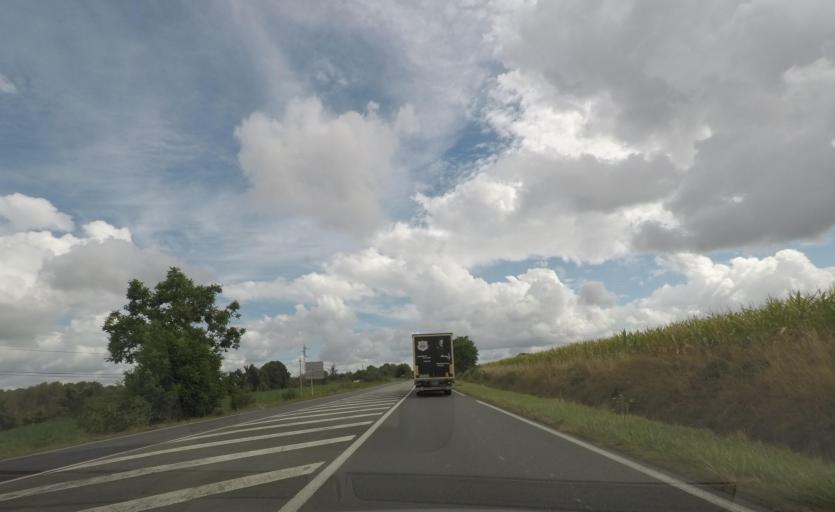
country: FR
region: Pays de la Loire
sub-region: Departement de Maine-et-Loire
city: Corze
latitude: 47.5589
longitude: -0.3753
